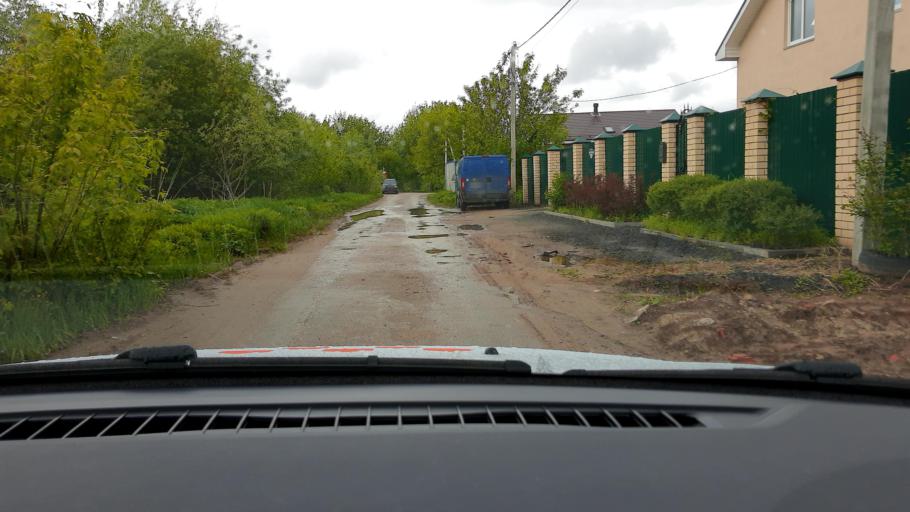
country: RU
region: Nizjnij Novgorod
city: Afonino
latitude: 56.2707
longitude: 44.0987
